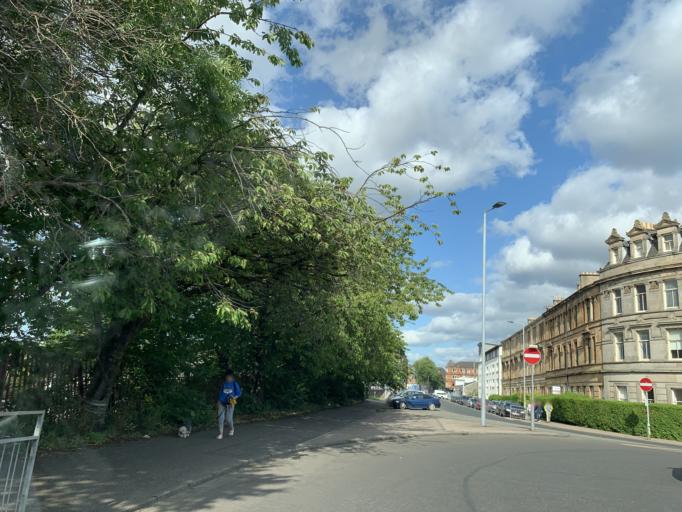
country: GB
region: Scotland
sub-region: Glasgow City
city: Glasgow
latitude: 55.8378
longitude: -4.2722
